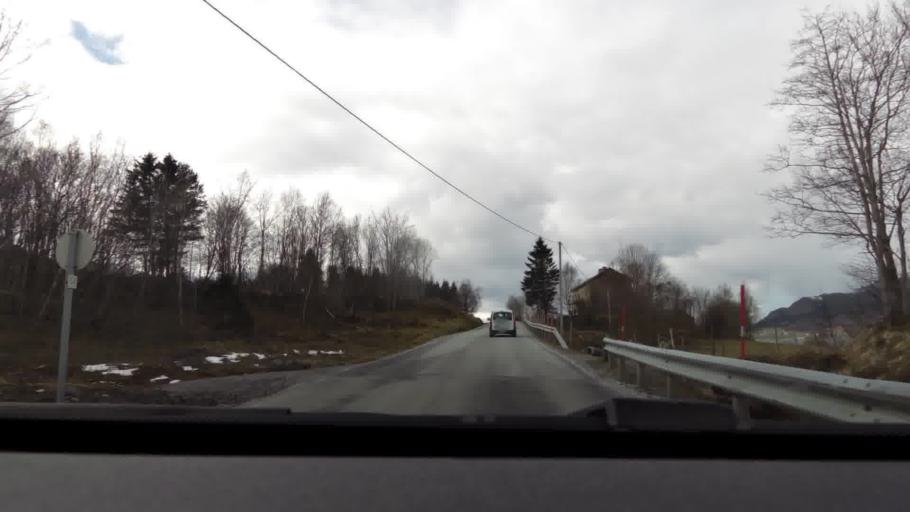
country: NO
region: More og Romsdal
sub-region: Gjemnes
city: Batnfjordsora
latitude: 62.9533
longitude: 7.6538
